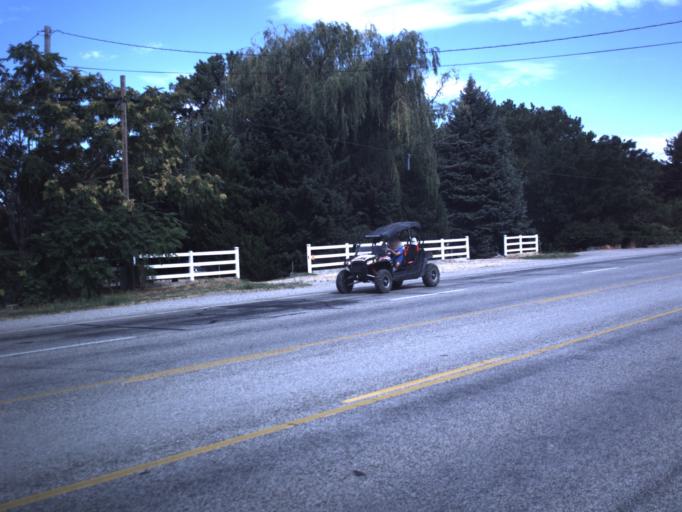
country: US
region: Utah
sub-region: Box Elder County
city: Willard
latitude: 41.3946
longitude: -112.0343
